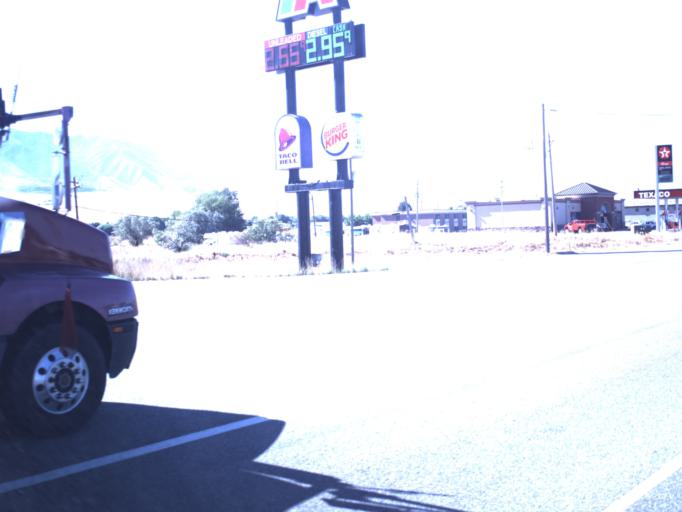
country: US
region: Utah
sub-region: Tooele County
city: Stansbury park
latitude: 40.6896
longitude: -112.2651
